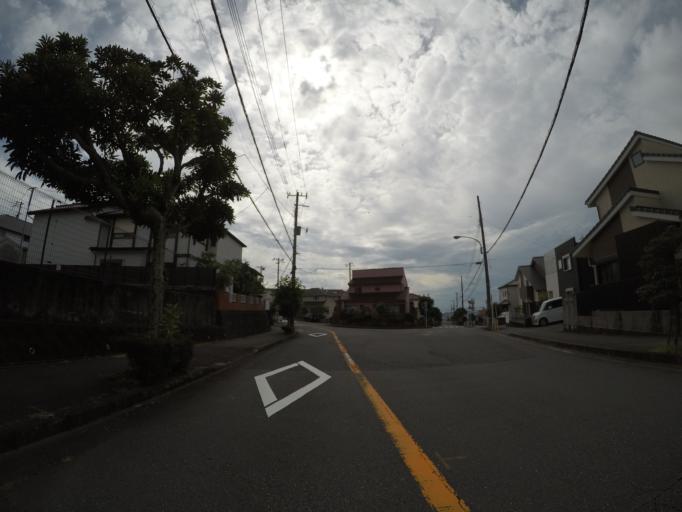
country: JP
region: Shizuoka
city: Fuji
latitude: 35.1846
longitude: 138.7177
